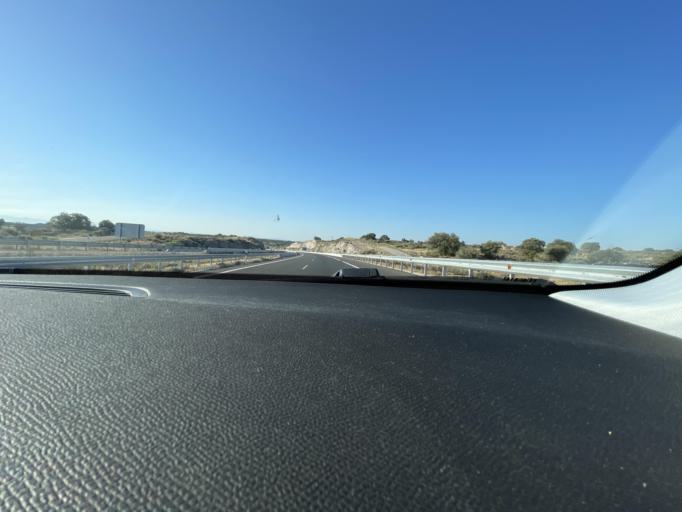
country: ES
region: Castille and Leon
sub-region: Provincia de Salamanca
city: Fuentes de Onoro
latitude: 40.6033
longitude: -6.8133
